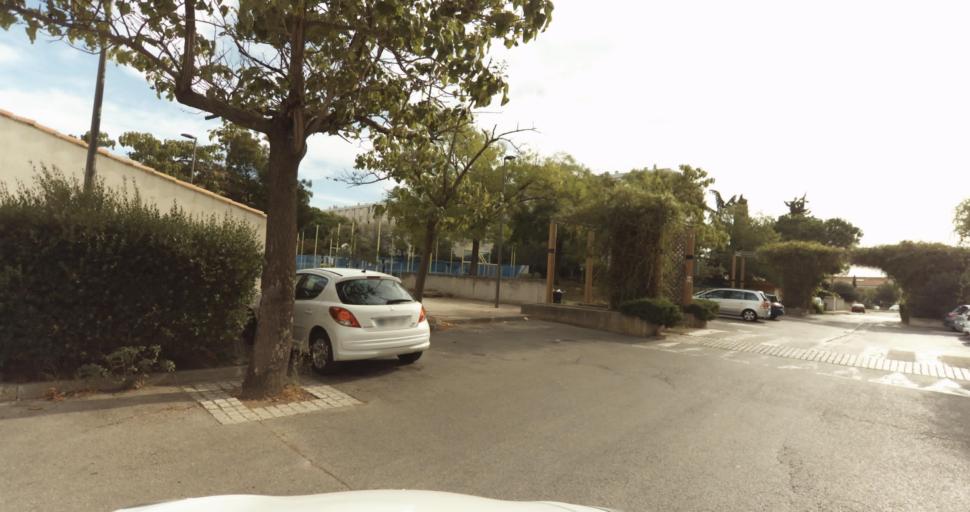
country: FR
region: Provence-Alpes-Cote d'Azur
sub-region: Departement des Bouches-du-Rhone
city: Miramas
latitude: 43.5878
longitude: 5.0066
